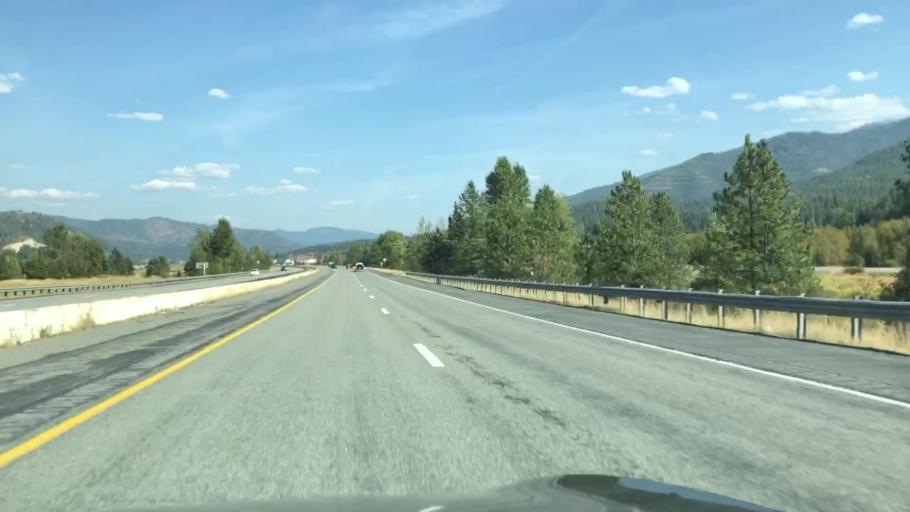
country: US
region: Idaho
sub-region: Shoshone County
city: Pinehurst
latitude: 47.5470
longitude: -116.2150
